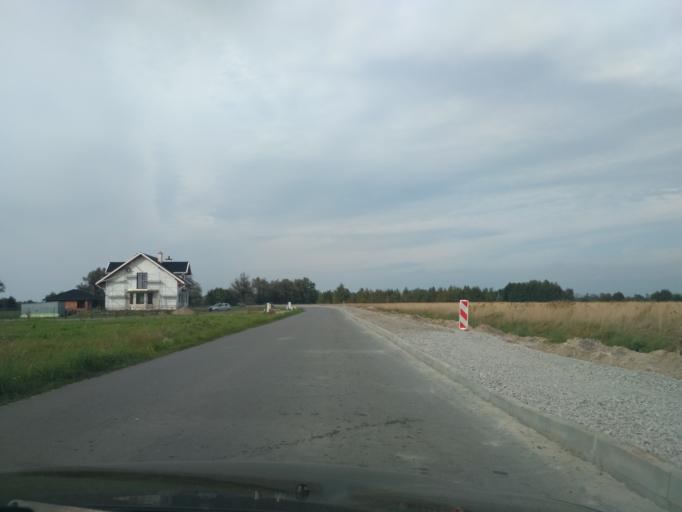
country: PL
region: Subcarpathian Voivodeship
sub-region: Powiat rzeszowski
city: Swilcza
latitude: 50.0824
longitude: 21.9129
